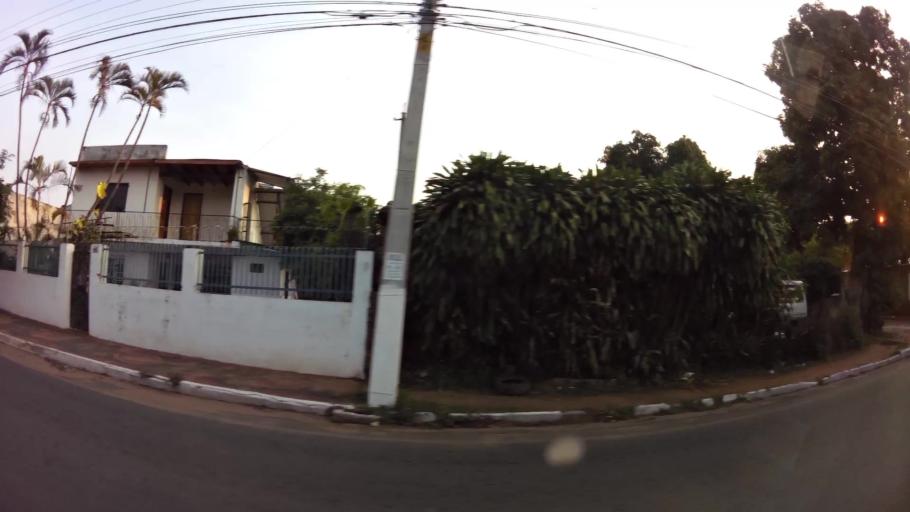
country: PY
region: Central
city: Lambare
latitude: -25.3567
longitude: -57.5998
